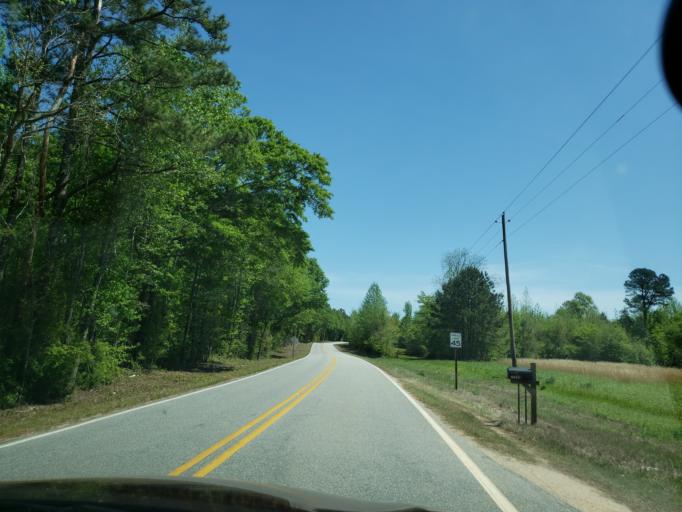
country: US
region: Alabama
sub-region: Tallapoosa County
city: Camp Hill
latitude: 32.6989
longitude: -85.6618
